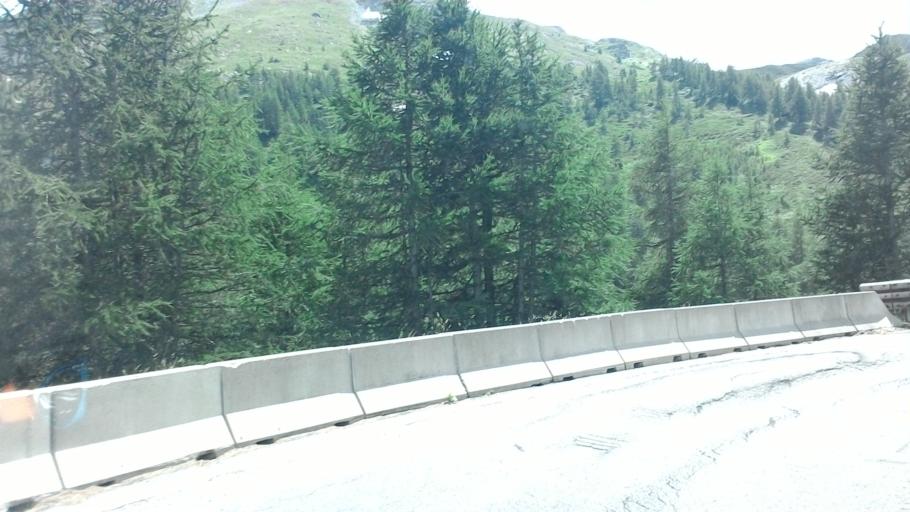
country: IT
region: Aosta Valley
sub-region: Valle d'Aosta
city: La Thuile
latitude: 45.7007
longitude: 6.9071
